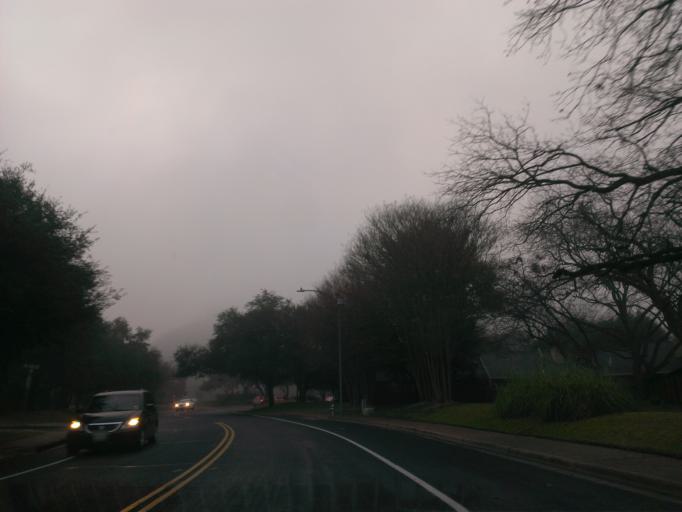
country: US
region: Texas
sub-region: Williamson County
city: Jollyville
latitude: 30.3723
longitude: -97.7876
